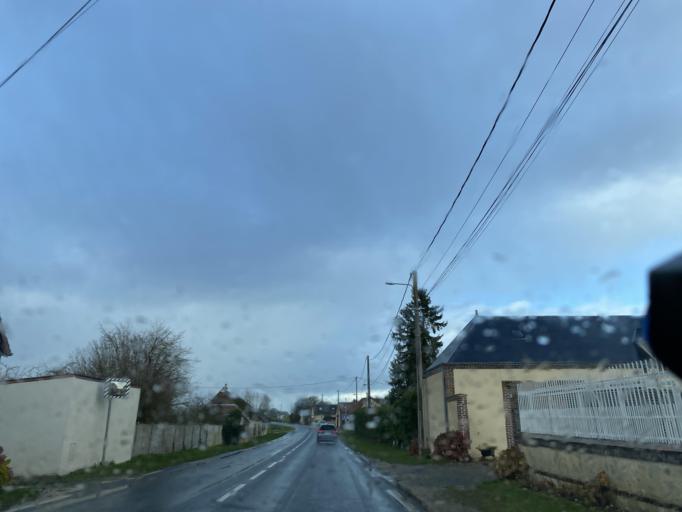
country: FR
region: Centre
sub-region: Departement d'Eure-et-Loir
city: Chateauneuf-en-Thymerais
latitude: 48.5511
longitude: 1.2931
